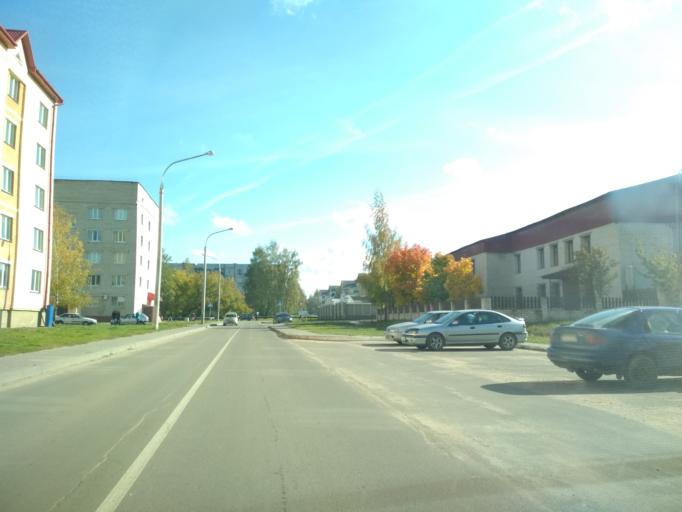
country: BY
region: Minsk
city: Mar''ina Horka
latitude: 53.5024
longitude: 28.1645
